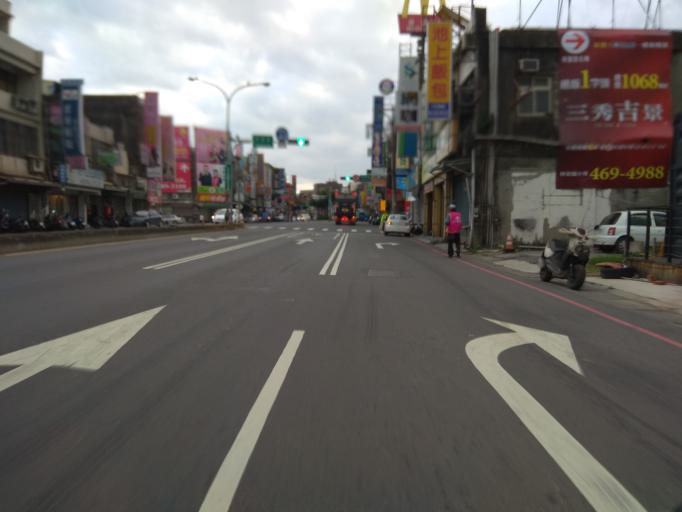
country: TW
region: Taiwan
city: Daxi
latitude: 24.9010
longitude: 121.2112
